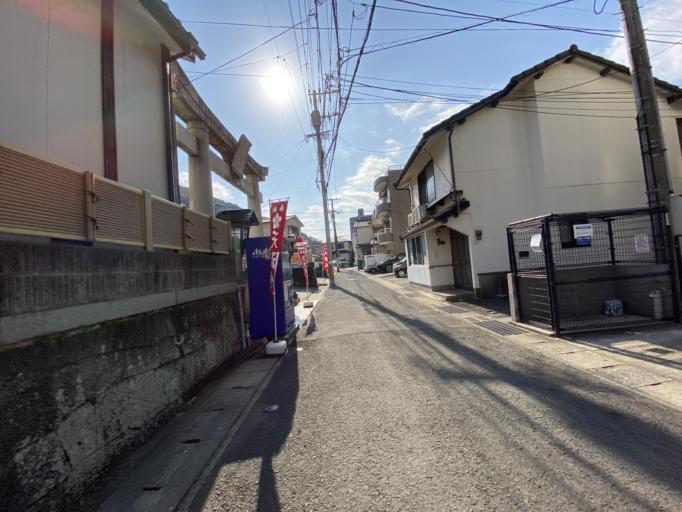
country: JP
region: Nagasaki
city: Nagasaki-shi
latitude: 32.7509
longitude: 129.8852
